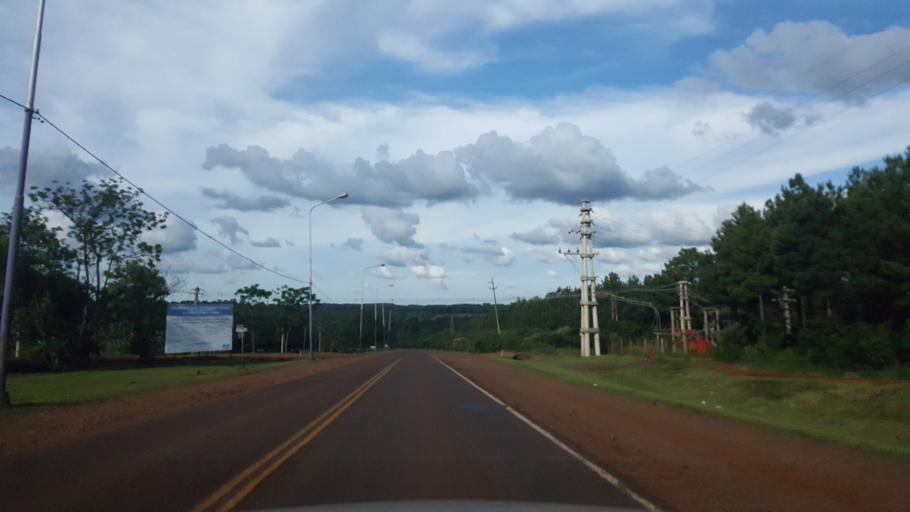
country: AR
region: Misiones
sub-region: Departamento de San Ignacio
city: San Ignacio
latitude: -27.2566
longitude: -55.5267
